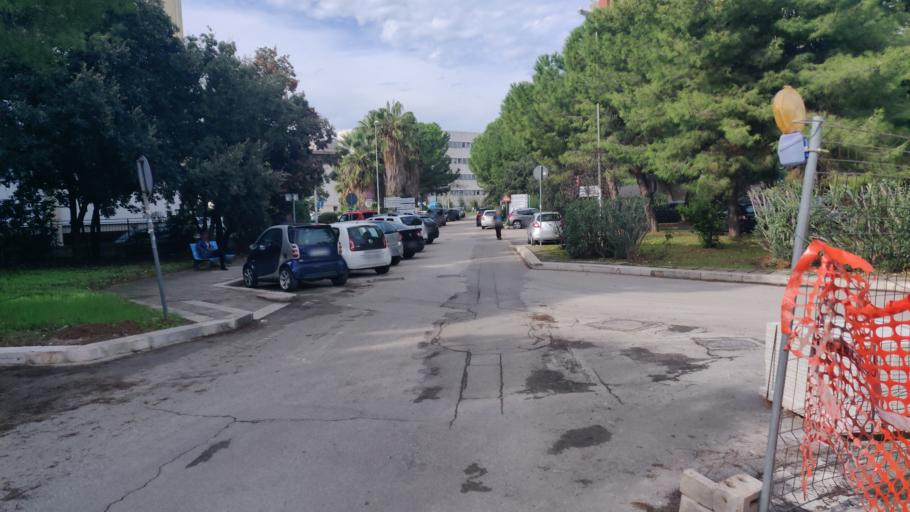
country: IT
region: Apulia
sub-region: Provincia di Bari
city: Bari
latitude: 41.1088
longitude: 16.8813
